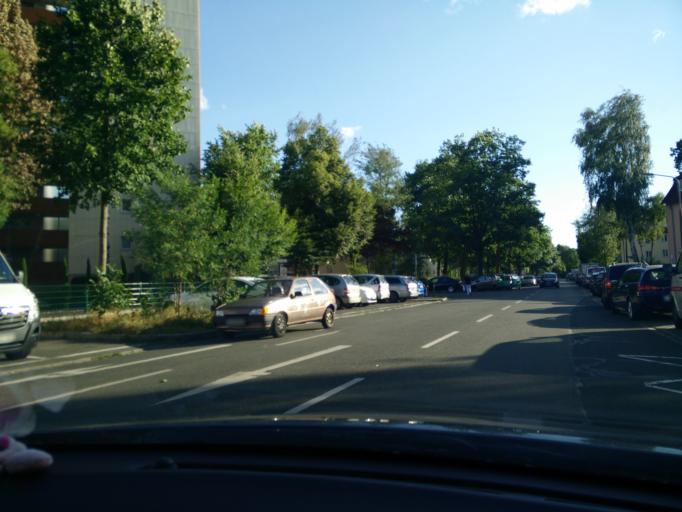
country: DE
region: Bavaria
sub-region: Regierungsbezirk Mittelfranken
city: Wendelstein
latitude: 49.4015
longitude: 11.1335
